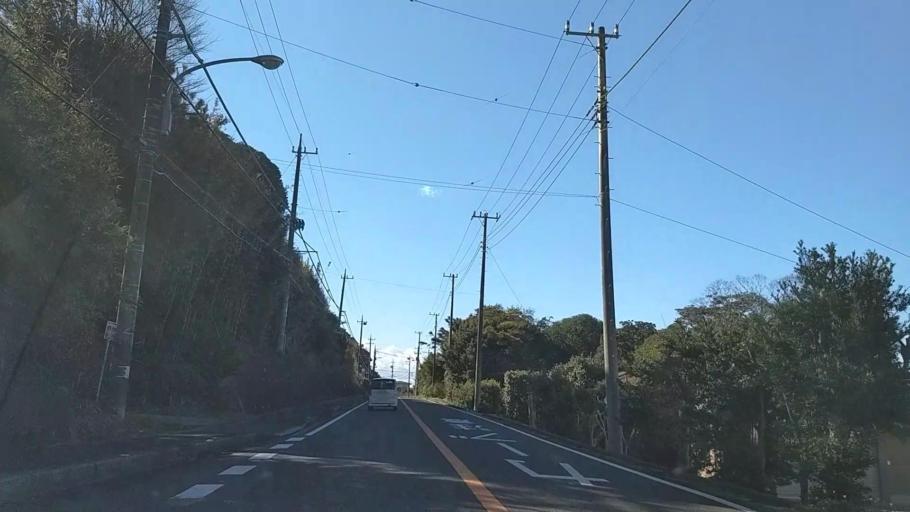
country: JP
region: Chiba
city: Tateyama
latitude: 34.9505
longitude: 139.8363
